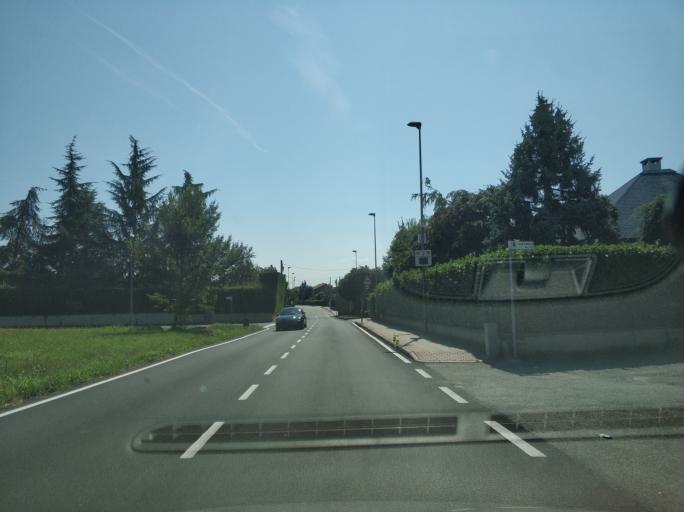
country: IT
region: Piedmont
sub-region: Provincia di Torino
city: San Francesco al Campo
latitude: 45.2334
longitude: 7.6402
